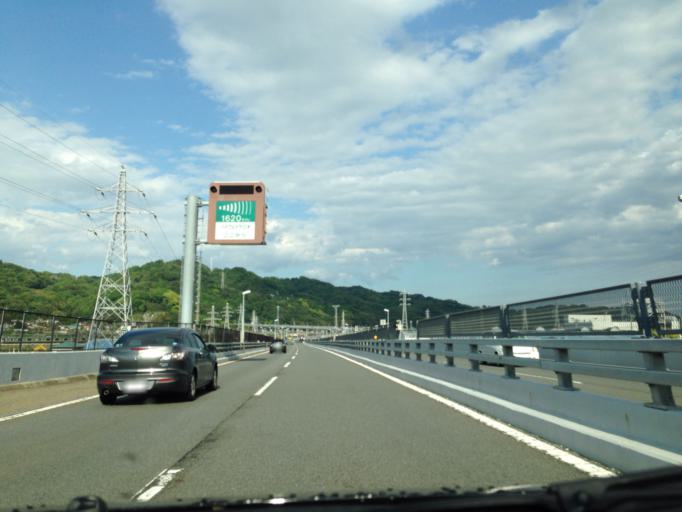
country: JP
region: Kanagawa
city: Odawara
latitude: 35.2902
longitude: 139.1910
